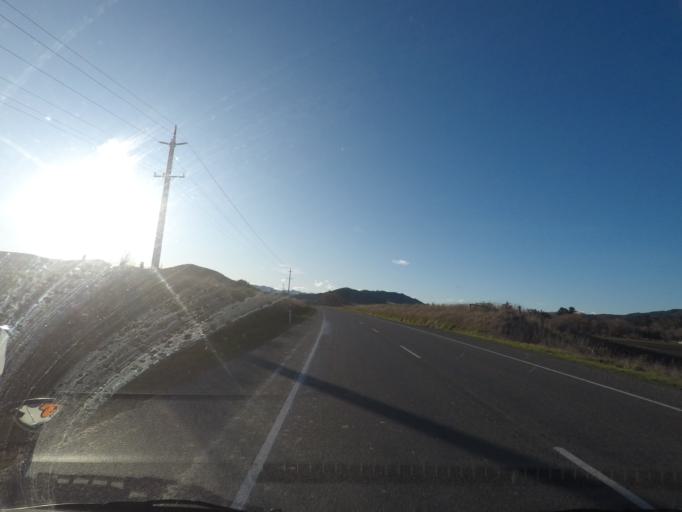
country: NZ
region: Canterbury
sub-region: Kaikoura District
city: Kaikoura
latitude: -42.6971
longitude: 173.3015
